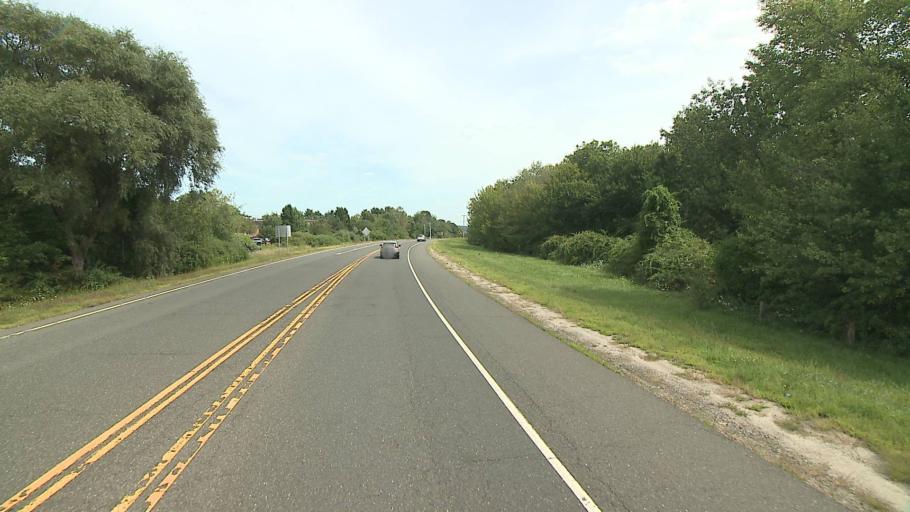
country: US
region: Connecticut
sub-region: Litchfield County
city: Oakville
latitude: 41.6076
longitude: -73.0883
